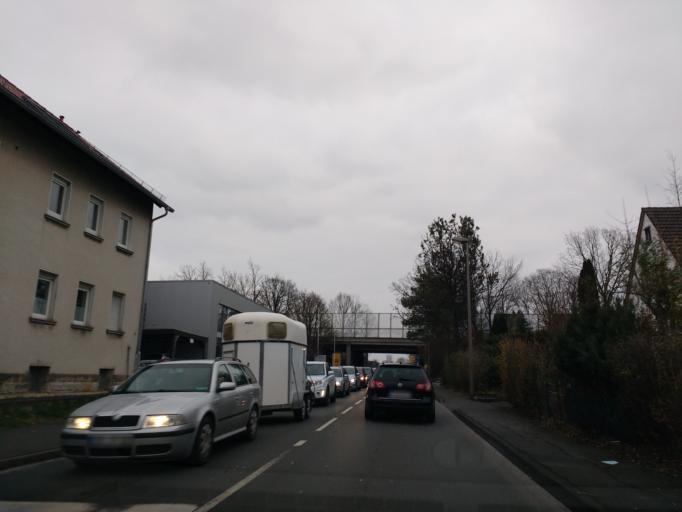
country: DE
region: Hesse
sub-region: Regierungsbezirk Kassel
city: Baunatal
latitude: 51.2279
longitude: 9.4234
